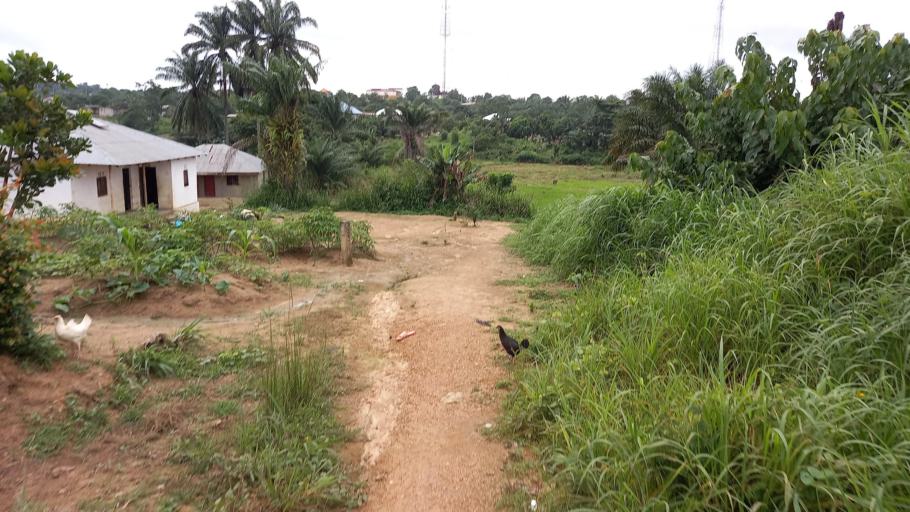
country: SL
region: Eastern Province
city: Kailahun
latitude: 8.2888
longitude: -10.5696
